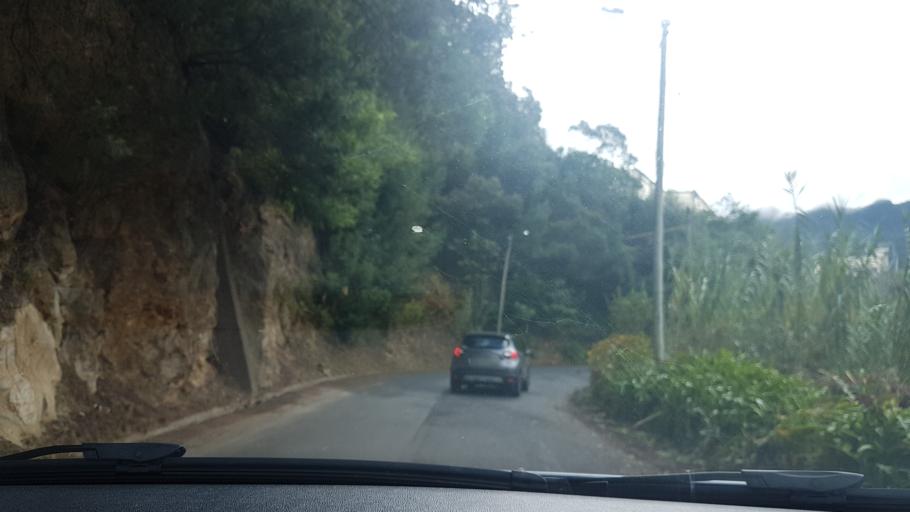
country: PT
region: Madeira
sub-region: Sao Vicente
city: Sao Vicente
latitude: 32.7774
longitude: -17.0286
